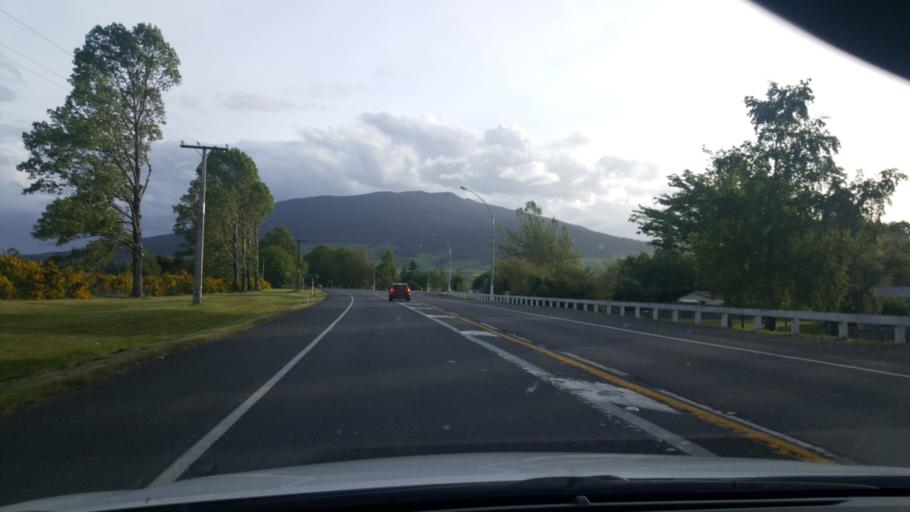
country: NZ
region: Waikato
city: Turangi
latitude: -38.9950
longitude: 175.8059
